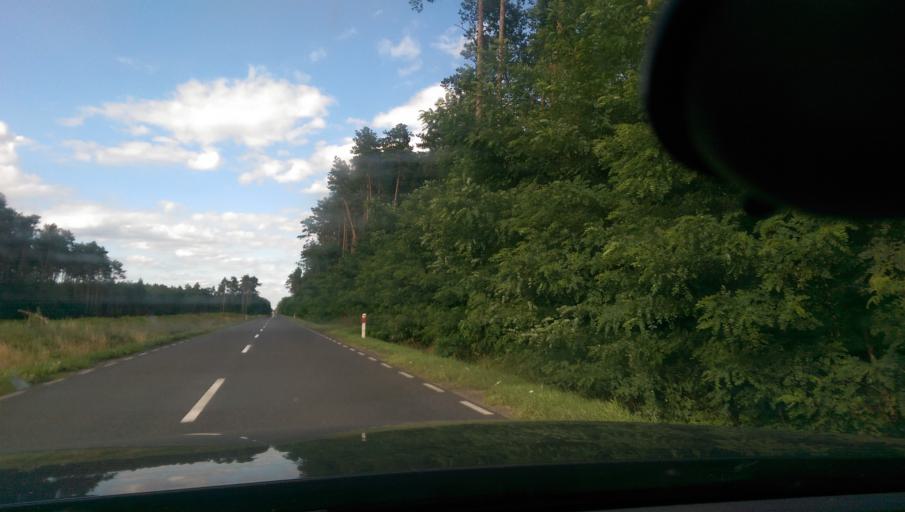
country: PL
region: Lubusz
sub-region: Powiat slubicki
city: Osno Lubuskie
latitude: 52.5116
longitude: 14.9136
